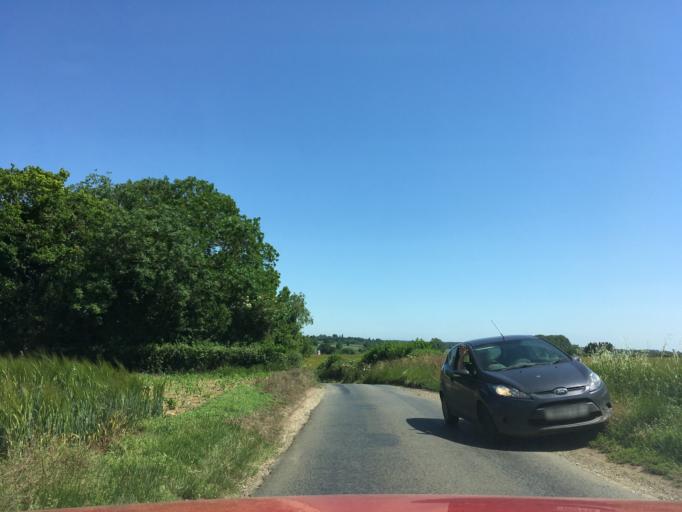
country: GB
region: England
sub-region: Northamptonshire
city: Brackley
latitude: 52.0033
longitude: -1.0947
